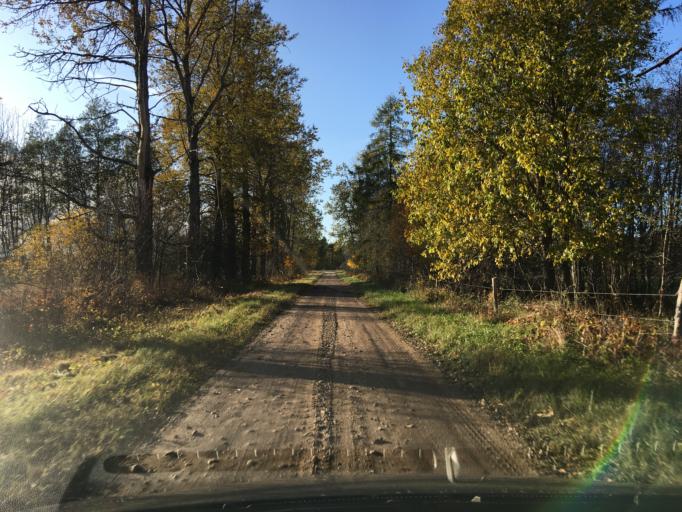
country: EE
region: Laeaene
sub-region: Lihula vald
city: Lihula
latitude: 58.5650
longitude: 23.7889
